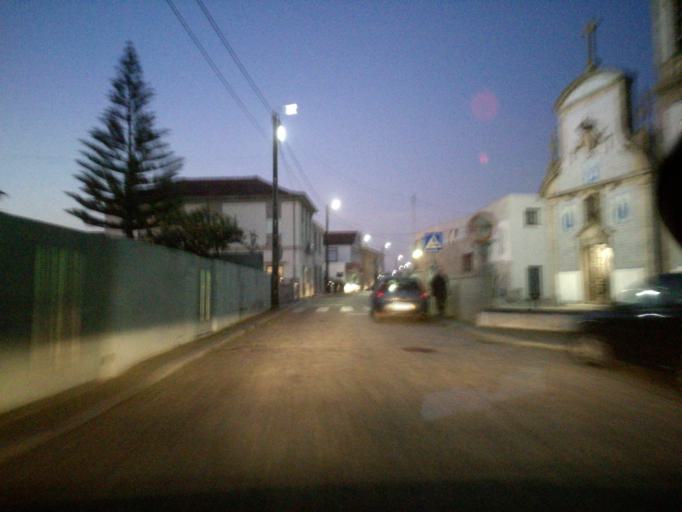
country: PT
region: Porto
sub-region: Maia
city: Nogueira
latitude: 41.2392
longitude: -8.5870
